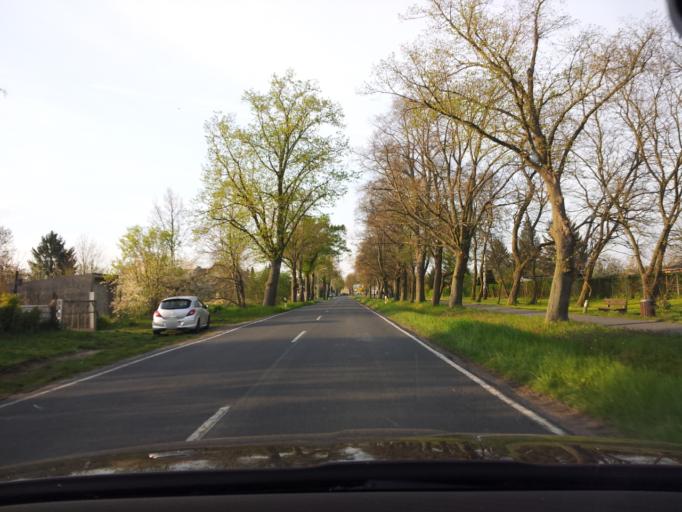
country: DE
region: Brandenburg
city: Dahme
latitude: 51.8612
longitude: 13.4171
